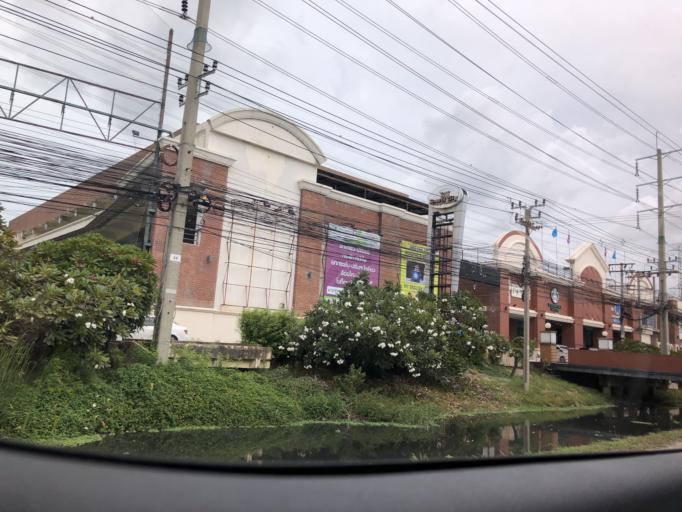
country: TH
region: Bangkok
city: Lak Si
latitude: 13.8794
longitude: 100.5504
